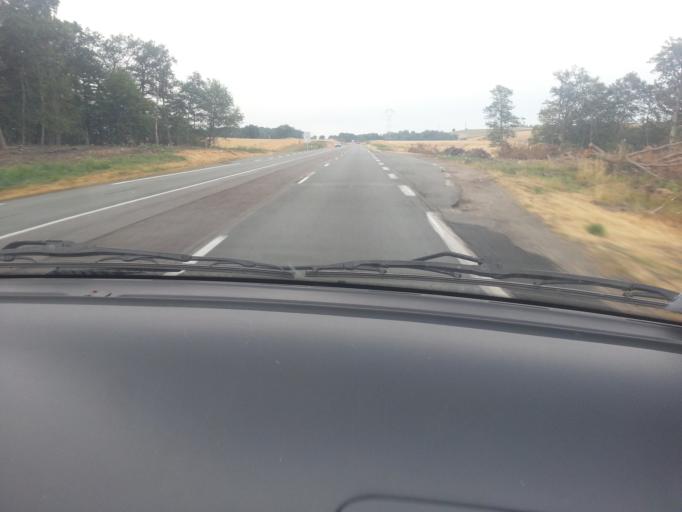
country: FR
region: Bourgogne
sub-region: Departement de Saone-et-Loire
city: Saint-Eusebe
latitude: 46.7106
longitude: 4.4278
